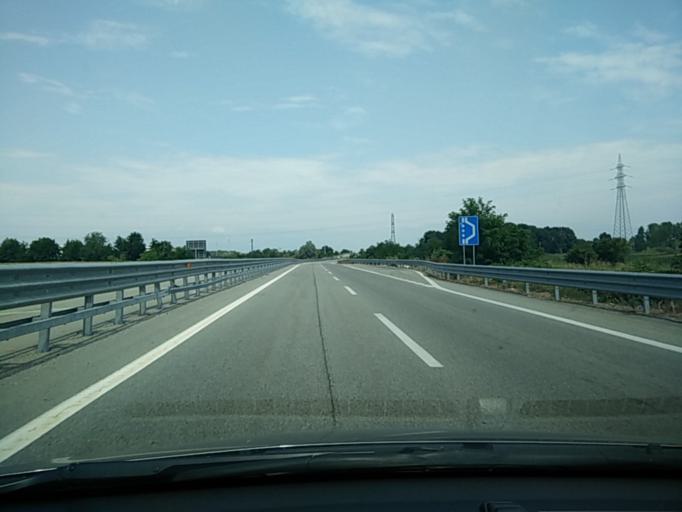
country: IT
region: Piedmont
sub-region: Provincia di Torino
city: Brandizzo
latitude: 45.1754
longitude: 7.8044
